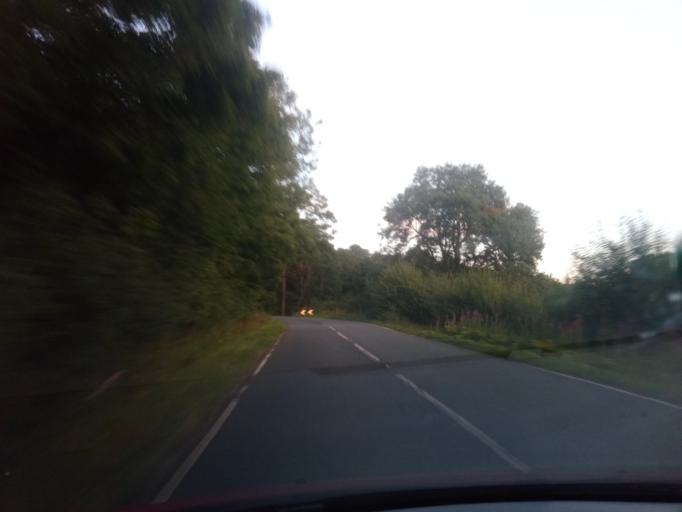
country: GB
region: England
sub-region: Northumberland
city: Bardon Mill
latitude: 54.9229
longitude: -2.3094
